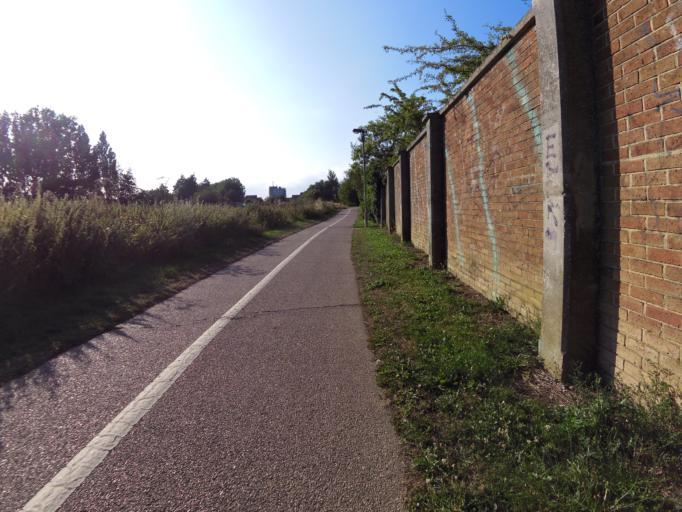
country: GB
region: England
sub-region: Essex
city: Chelmsford
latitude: 51.7290
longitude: 0.4823
